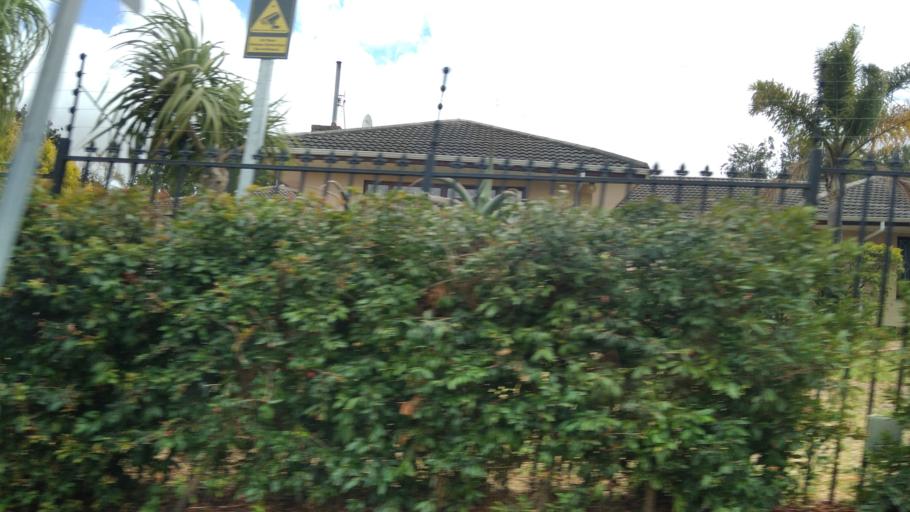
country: ZA
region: Western Cape
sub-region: City of Cape Town
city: Kraaifontein
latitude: -33.8222
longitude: 18.6575
